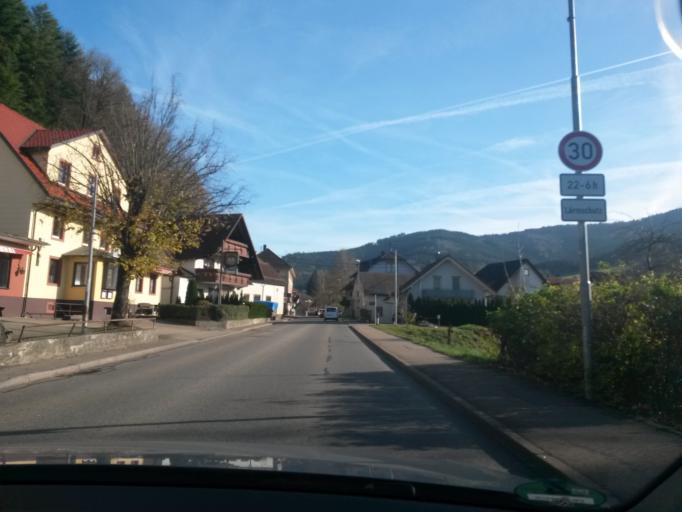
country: DE
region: Baden-Wuerttemberg
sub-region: Freiburg Region
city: Elzach
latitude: 48.1539
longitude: 8.0394
